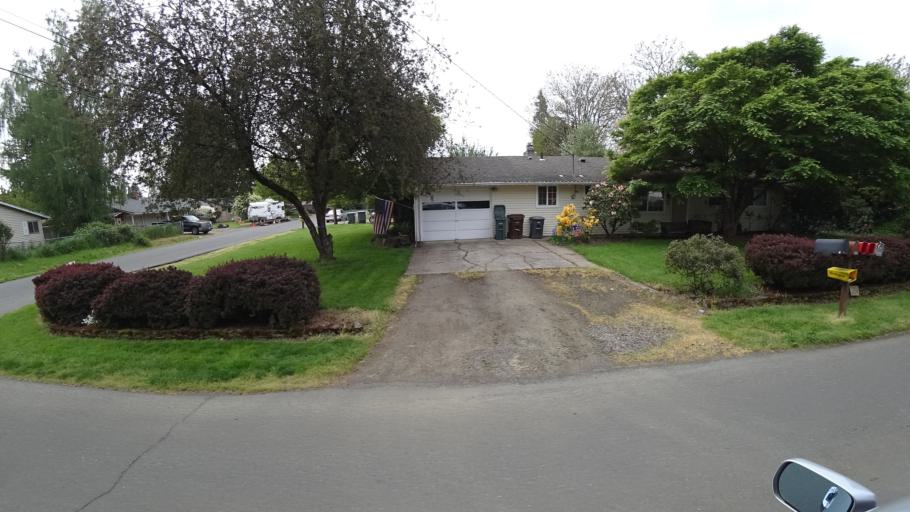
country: US
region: Oregon
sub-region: Washington County
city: Hillsboro
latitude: 45.5280
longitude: -122.9986
